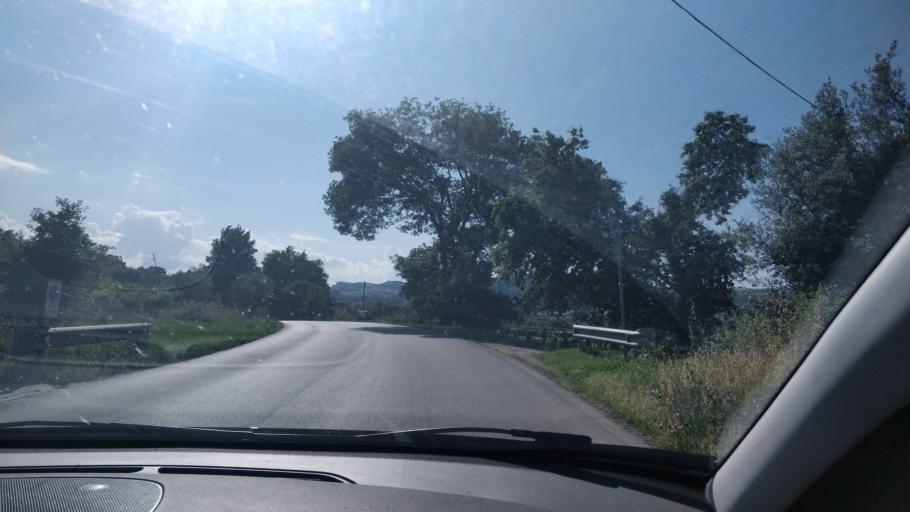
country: IT
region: The Marches
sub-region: Provincia di Ascoli Piceno
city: Cupra Marittima
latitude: 43.0355
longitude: 13.8430
